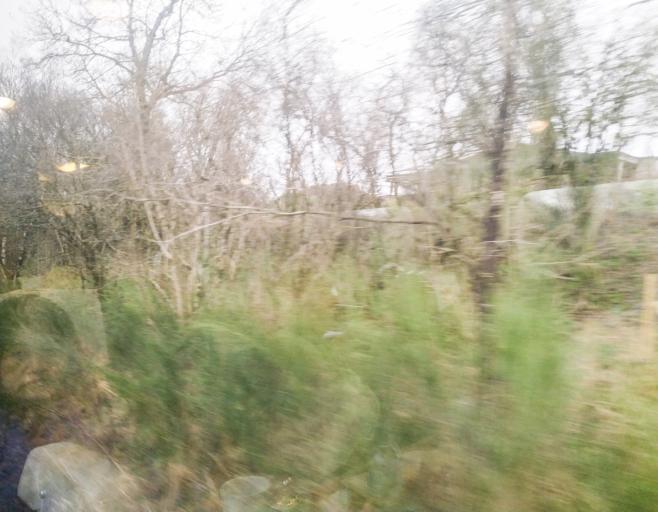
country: GB
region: Scotland
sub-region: Highland
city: Spean Bridge
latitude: 56.8890
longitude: -4.8659
